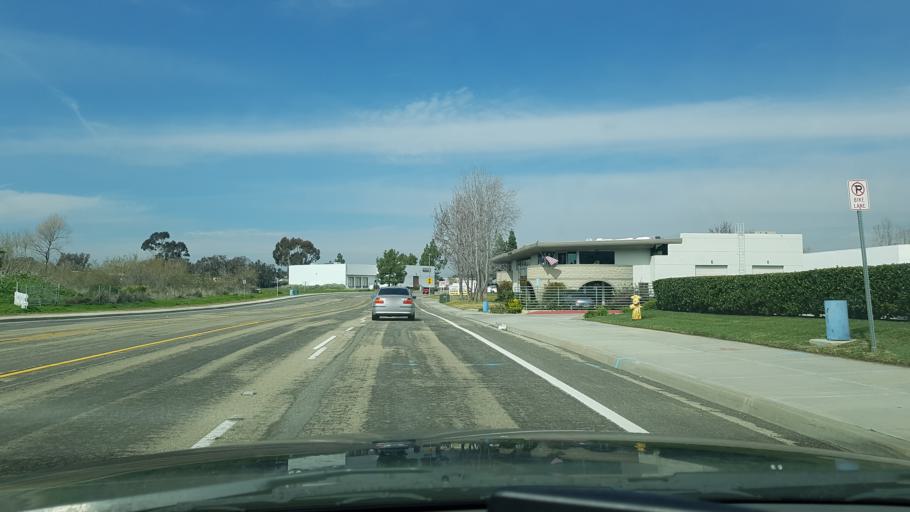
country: US
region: California
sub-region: San Diego County
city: Lake San Marcos
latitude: 33.1346
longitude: -117.1944
